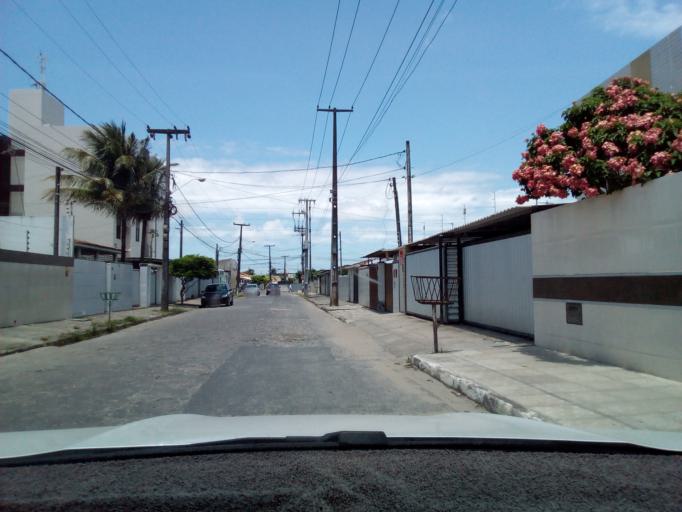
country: BR
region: Paraiba
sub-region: Joao Pessoa
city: Joao Pessoa
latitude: -7.1804
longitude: -34.8747
